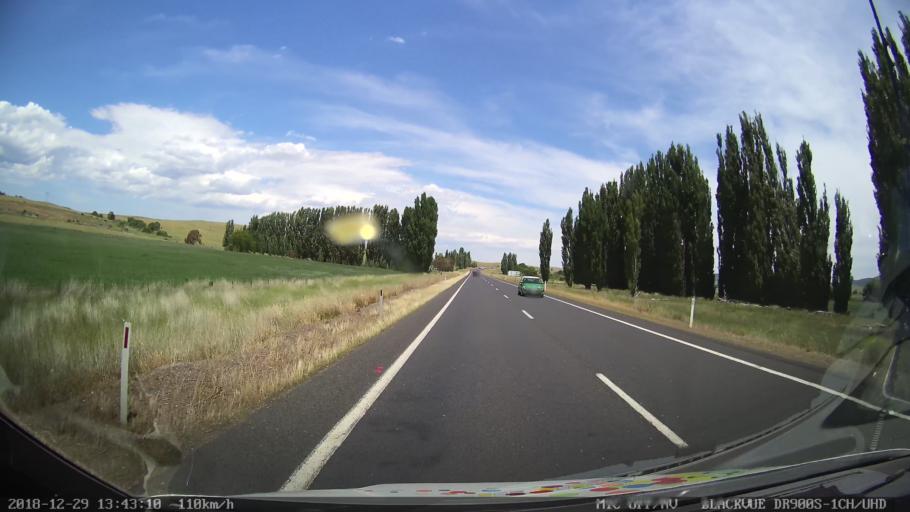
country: AU
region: New South Wales
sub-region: Cooma-Monaro
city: Cooma
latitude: -36.0683
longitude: 149.1586
